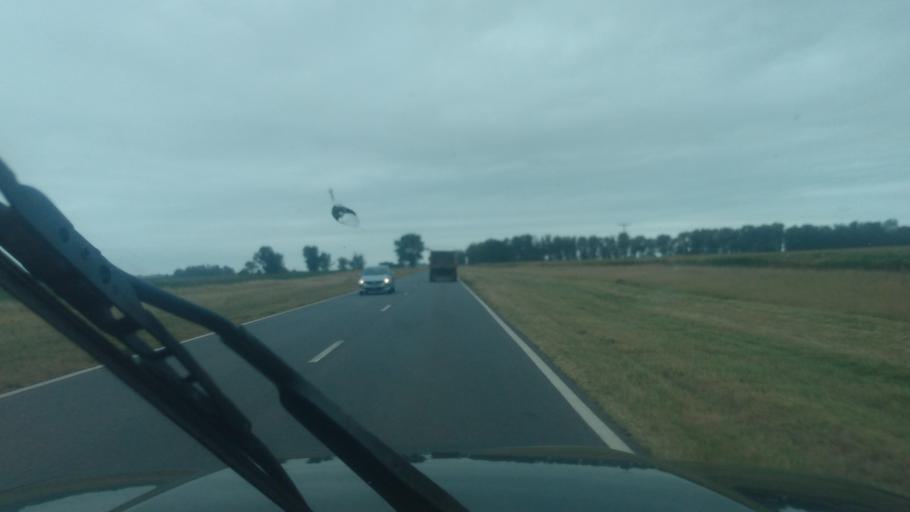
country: AR
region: Buenos Aires
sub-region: Partido de Nueve de Julio
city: Nueve de Julio
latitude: -35.4079
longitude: -60.7734
